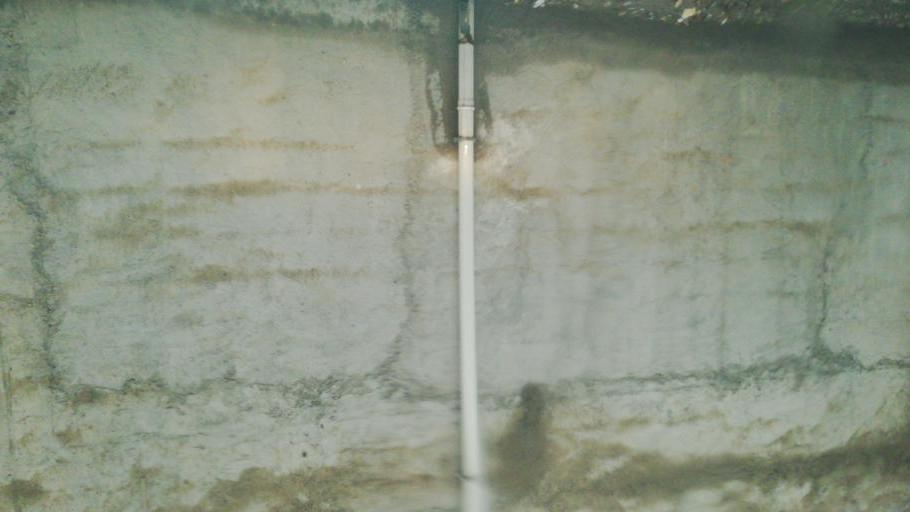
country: TR
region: Kahramanmaras
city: Kahramanmaras
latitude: 37.5588
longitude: 36.9609
